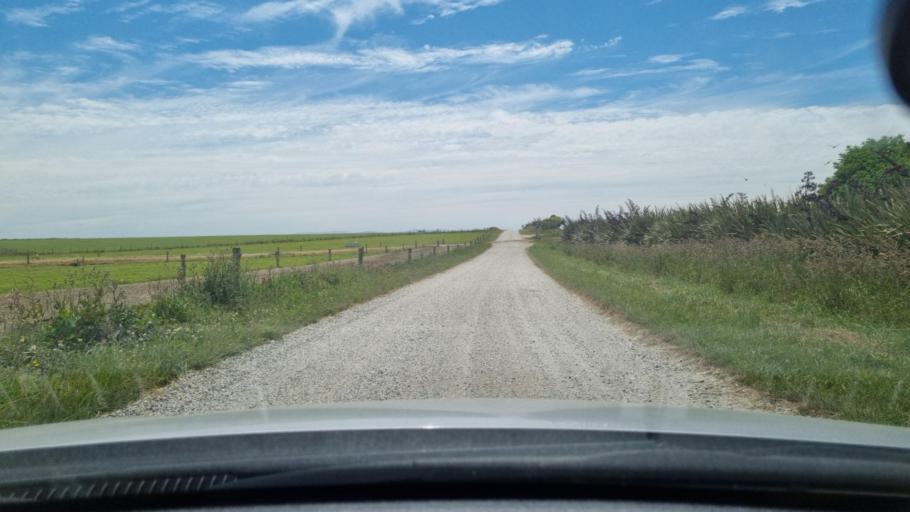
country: NZ
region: Southland
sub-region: Invercargill City
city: Invercargill
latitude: -46.4016
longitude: 168.2599
